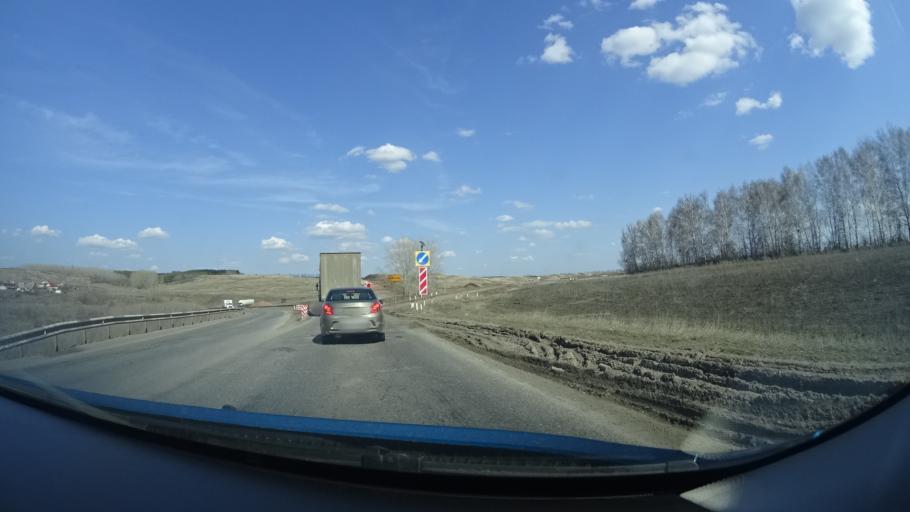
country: RU
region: Bashkortostan
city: Buzdyak
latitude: 54.6291
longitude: 54.4623
